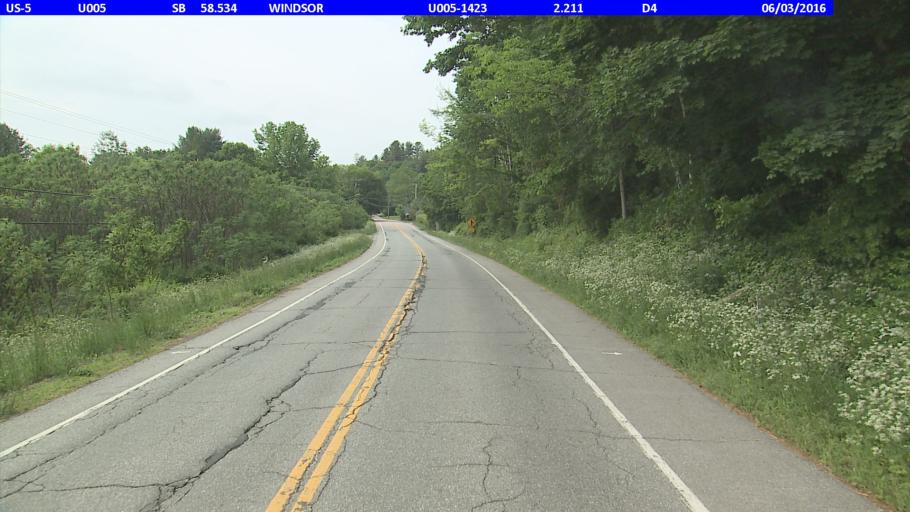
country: US
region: Vermont
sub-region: Windsor County
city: Windsor
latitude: 43.4601
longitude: -72.3936
